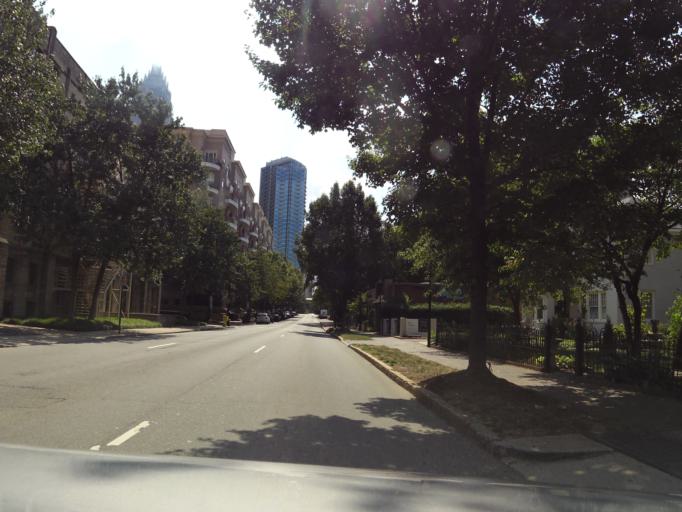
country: US
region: North Carolina
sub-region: Mecklenburg County
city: Charlotte
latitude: 35.2315
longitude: -80.8393
